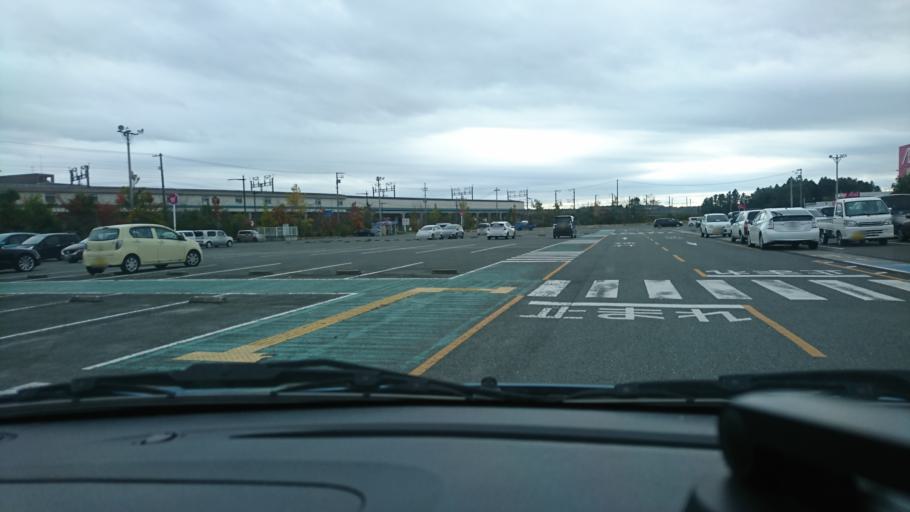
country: JP
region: Iwate
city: Ichinoseki
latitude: 38.7494
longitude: 141.0701
